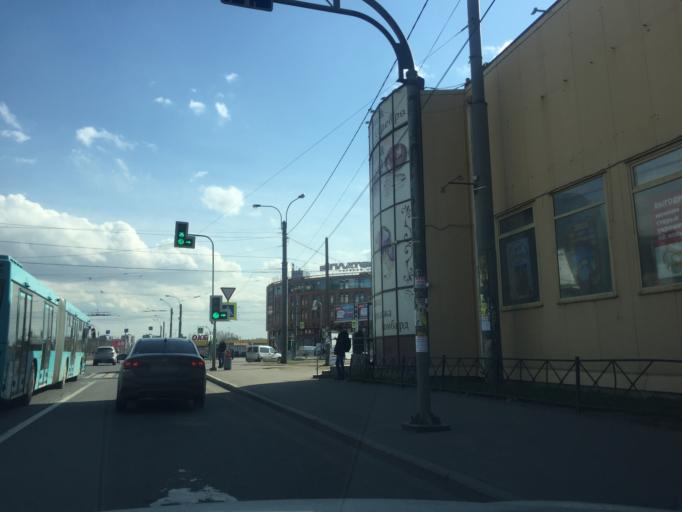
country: RU
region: St.-Petersburg
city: Krasnogvargeisky
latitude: 59.9340
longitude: 30.4352
